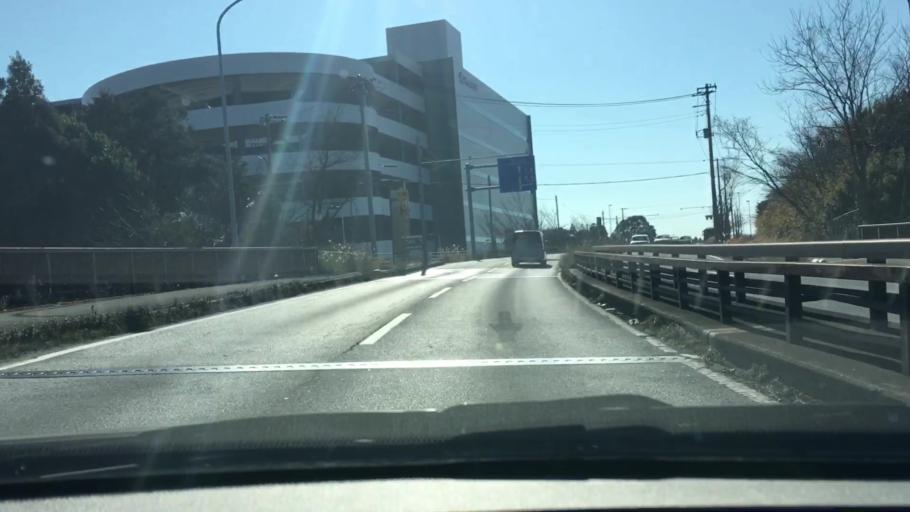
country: JP
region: Chiba
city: Narita
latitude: 35.7424
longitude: 140.4023
